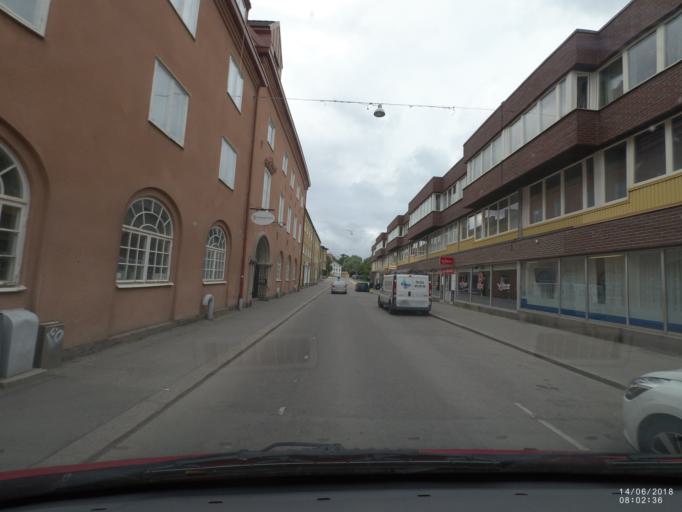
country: SE
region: Soedermanland
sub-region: Nykopings Kommun
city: Nykoping
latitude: 58.7542
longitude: 17.0149
